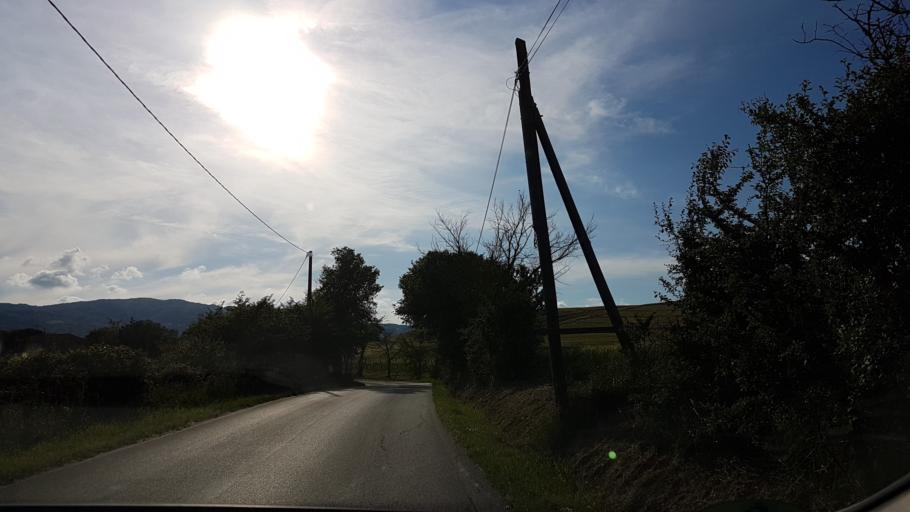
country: IT
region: Tuscany
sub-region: Province of Pisa
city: Lajatico
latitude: 43.4815
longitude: 10.6867
